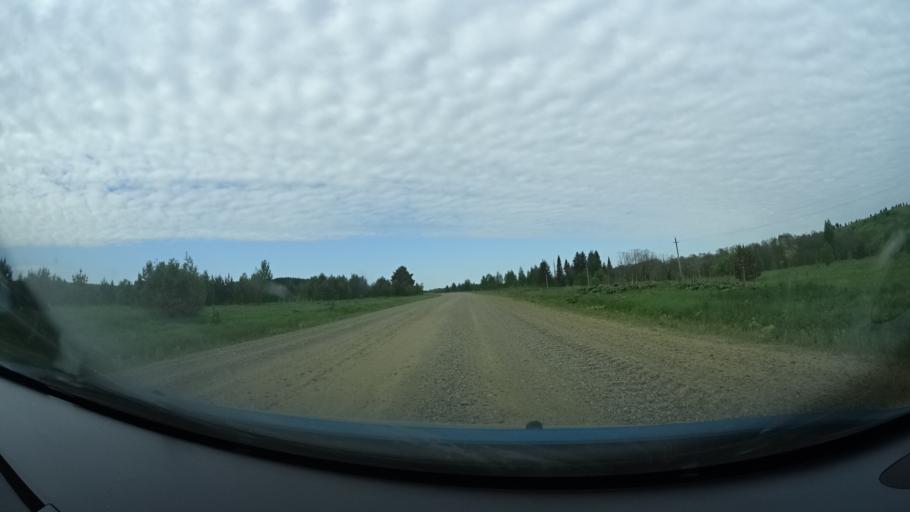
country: RU
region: Perm
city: Kuyeda
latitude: 56.5276
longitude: 55.6352
